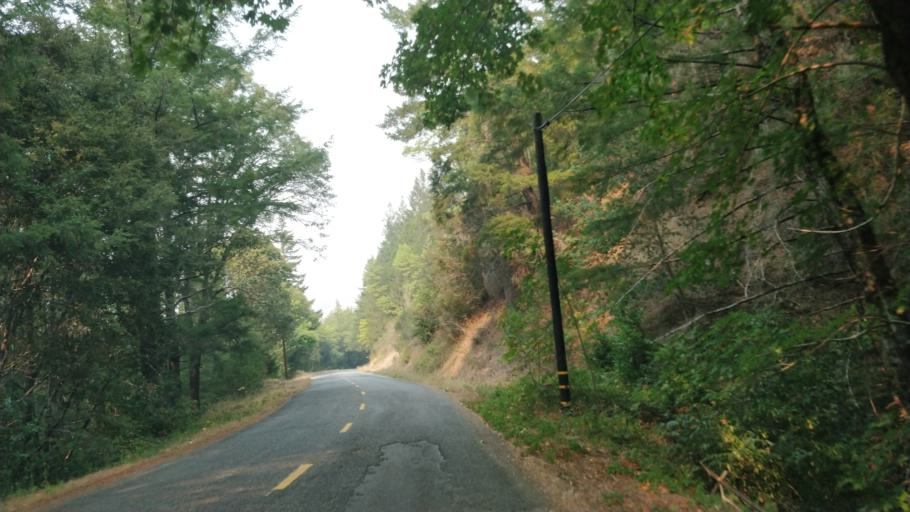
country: US
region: California
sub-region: Humboldt County
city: Rio Dell
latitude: 40.2348
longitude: -124.1364
